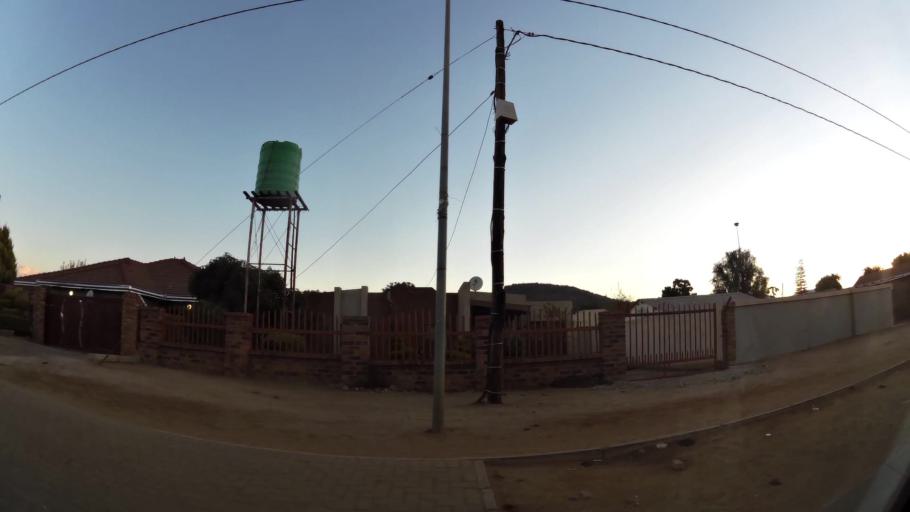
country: ZA
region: Limpopo
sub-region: Waterberg District Municipality
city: Mokopane
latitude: -24.1457
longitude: 28.9764
